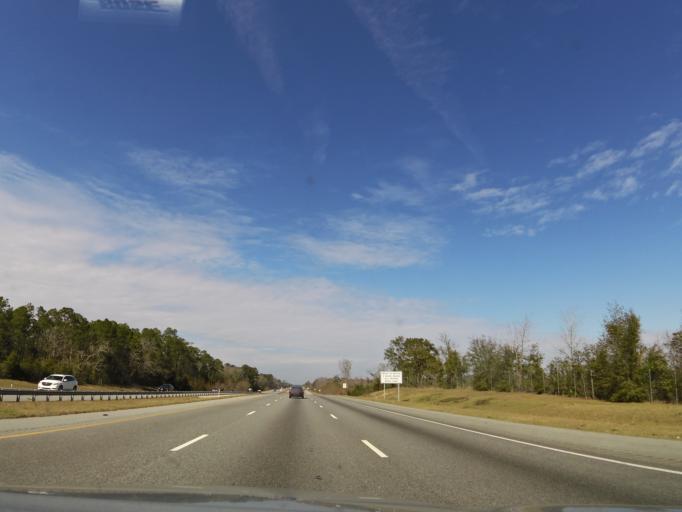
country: US
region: Georgia
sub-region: McIntosh County
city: Darien
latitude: 31.4340
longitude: -81.4438
